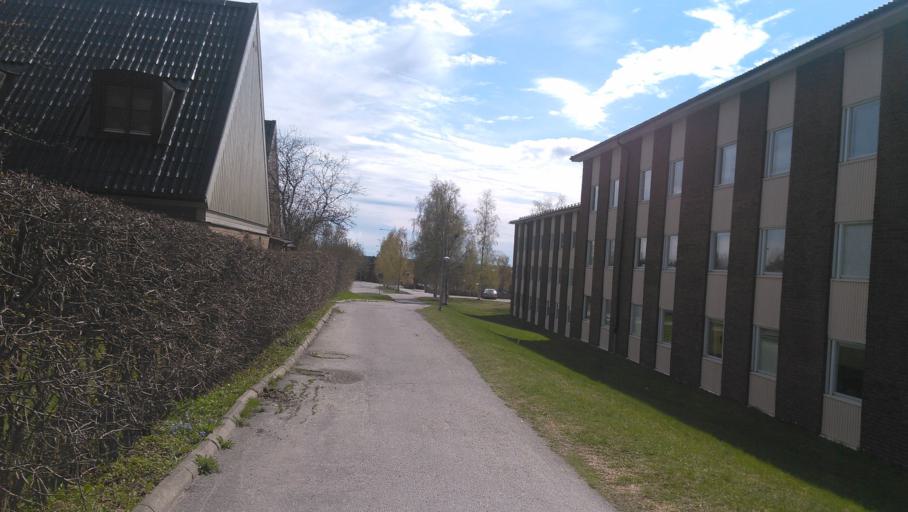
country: SE
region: Vaesterbotten
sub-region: Umea Kommun
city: Umea
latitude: 63.8008
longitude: 20.3168
